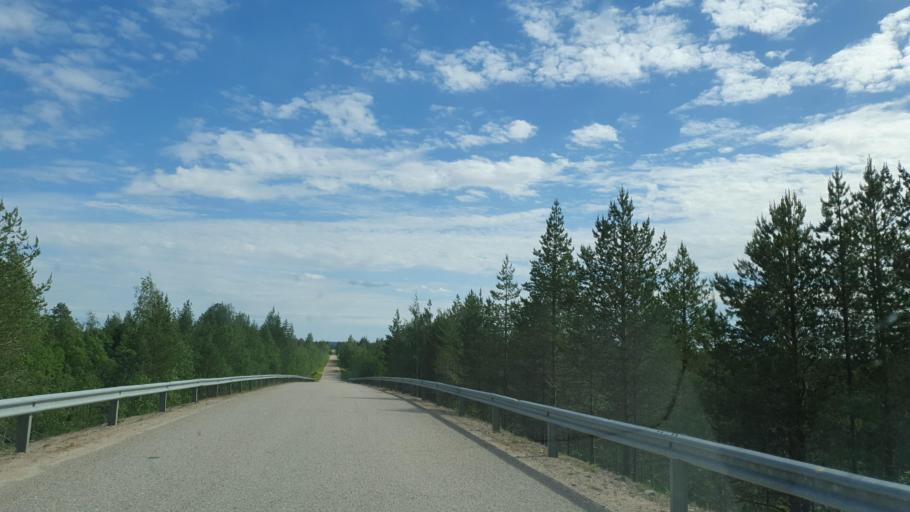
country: FI
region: Kainuu
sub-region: Kehys-Kainuu
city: Kuhmo
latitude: 64.4844
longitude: 29.5242
